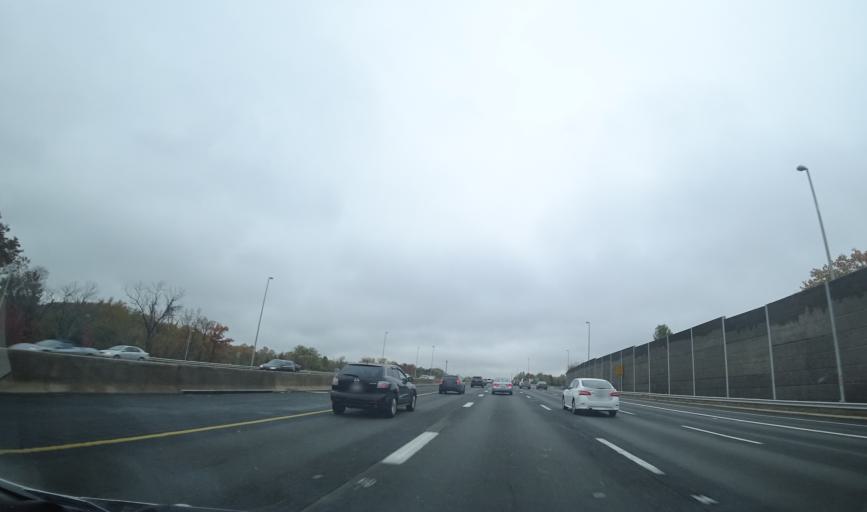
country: US
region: Virginia
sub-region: Fairfax County
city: Centreville
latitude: 38.8348
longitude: -77.4492
